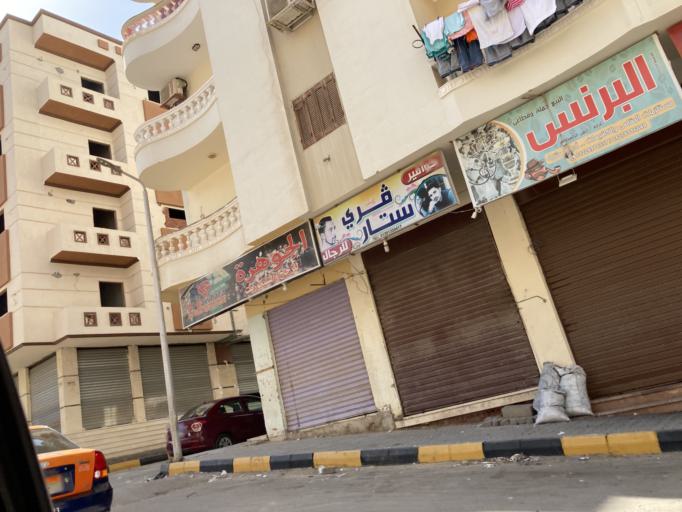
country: EG
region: Red Sea
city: Hurghada
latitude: 27.2507
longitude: 33.8319
